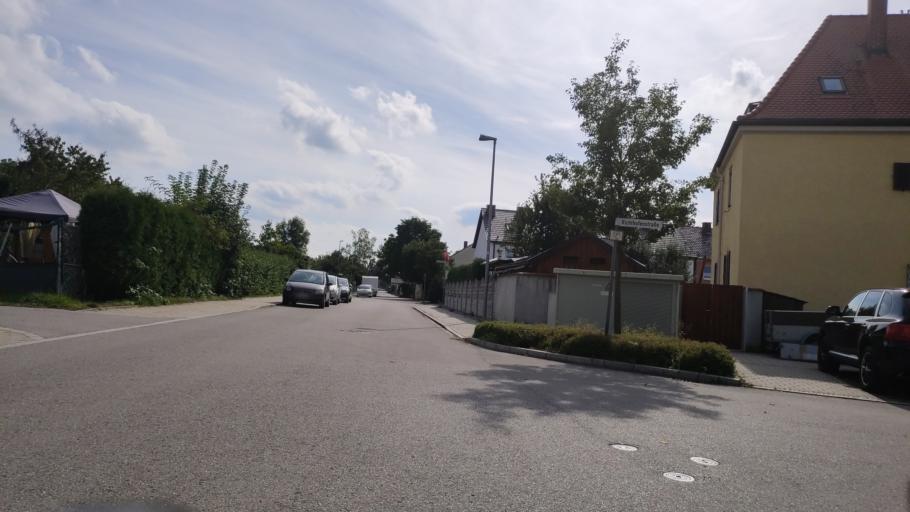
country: DE
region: Bavaria
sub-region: Swabia
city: Klosterlechfeld
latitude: 48.1717
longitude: 10.8416
